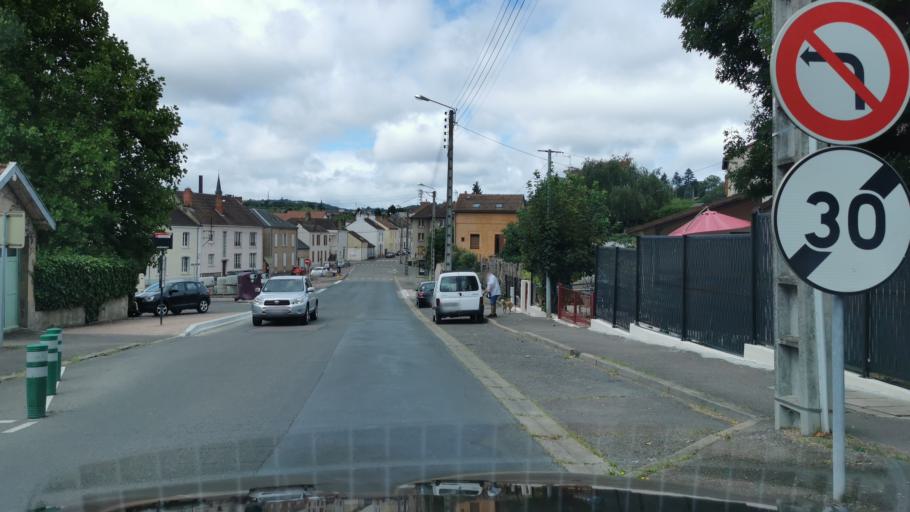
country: FR
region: Bourgogne
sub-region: Departement de Saone-et-Loire
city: Le Creusot
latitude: 46.8060
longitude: 4.4412
